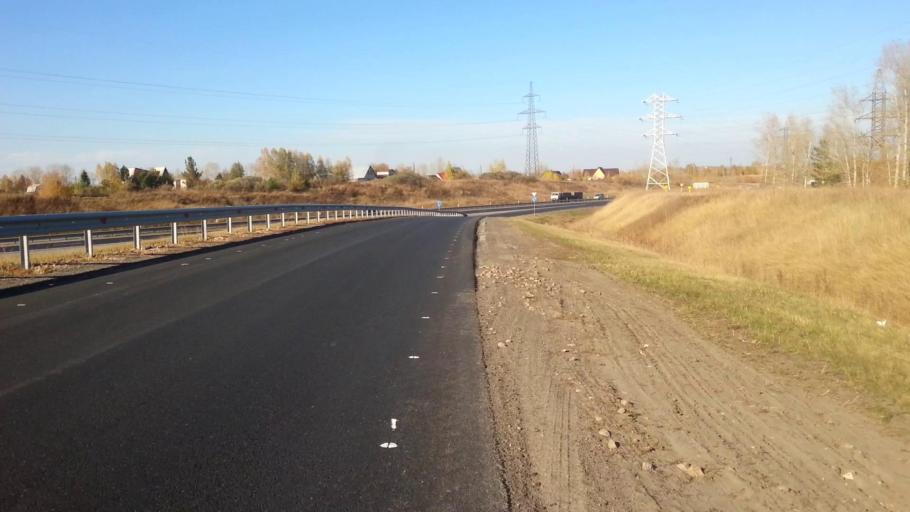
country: RU
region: Altai Krai
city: Sannikovo
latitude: 53.3413
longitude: 83.9389
